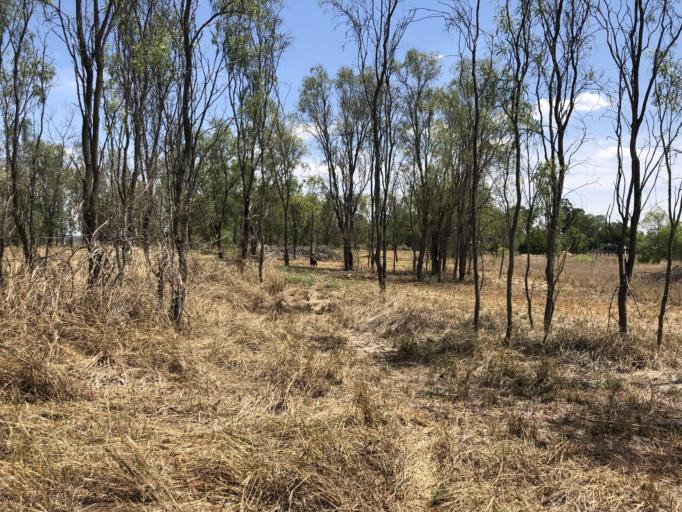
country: AU
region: Queensland
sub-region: Lockyer Valley
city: Gatton
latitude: -27.5850
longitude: 152.3468
